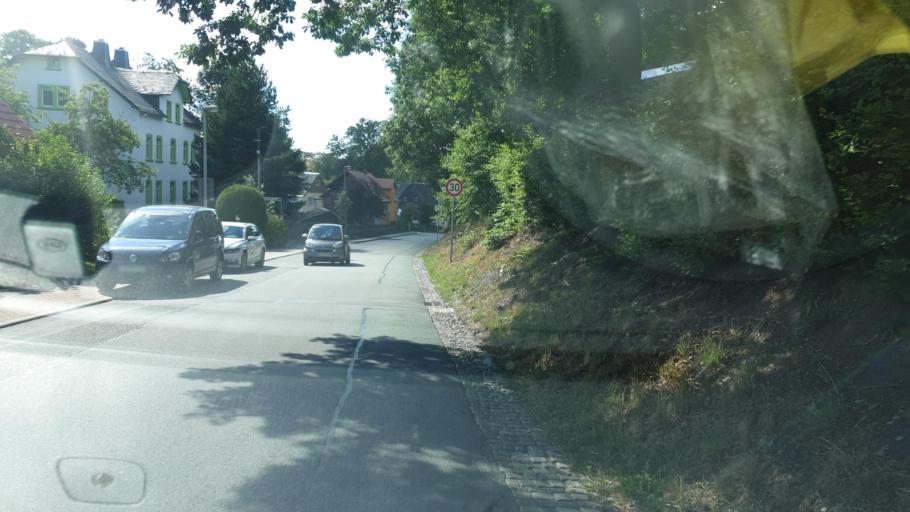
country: DE
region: Saxony
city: Burkhardtsdorf
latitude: 50.7562
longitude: 12.9187
